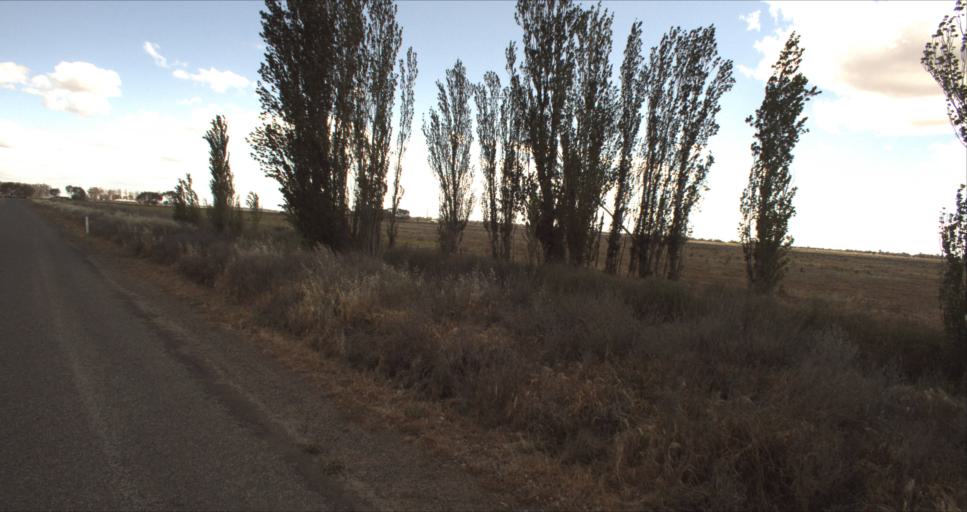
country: AU
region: New South Wales
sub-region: Leeton
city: Leeton
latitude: -34.5275
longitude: 146.2202
